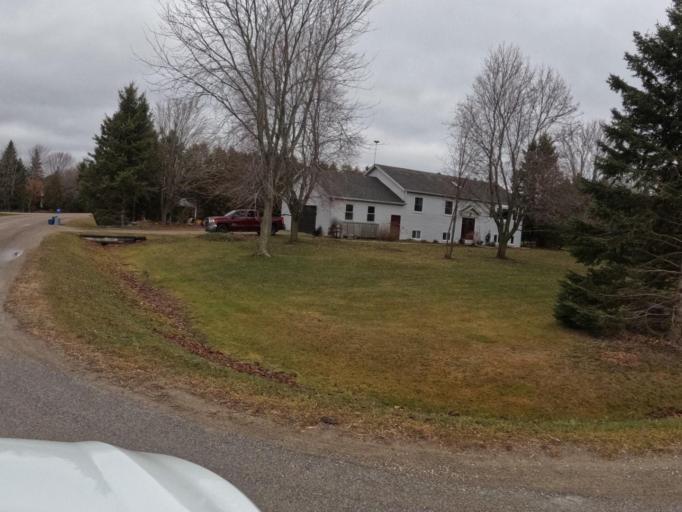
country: CA
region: Ontario
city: Shelburne
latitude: 43.9904
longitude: -80.3661
